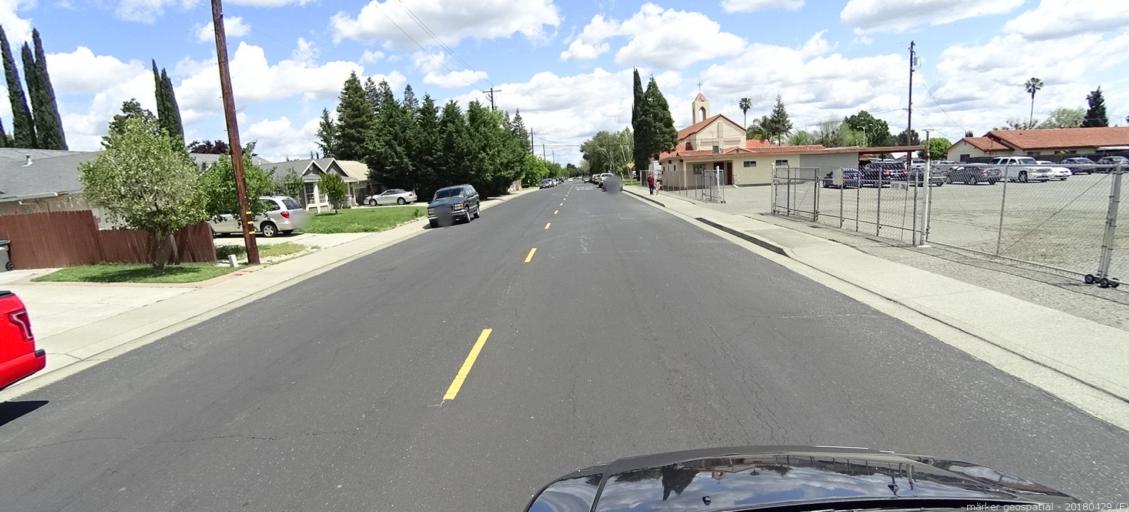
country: US
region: California
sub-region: Yolo County
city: West Sacramento
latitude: 38.5948
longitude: -121.5354
